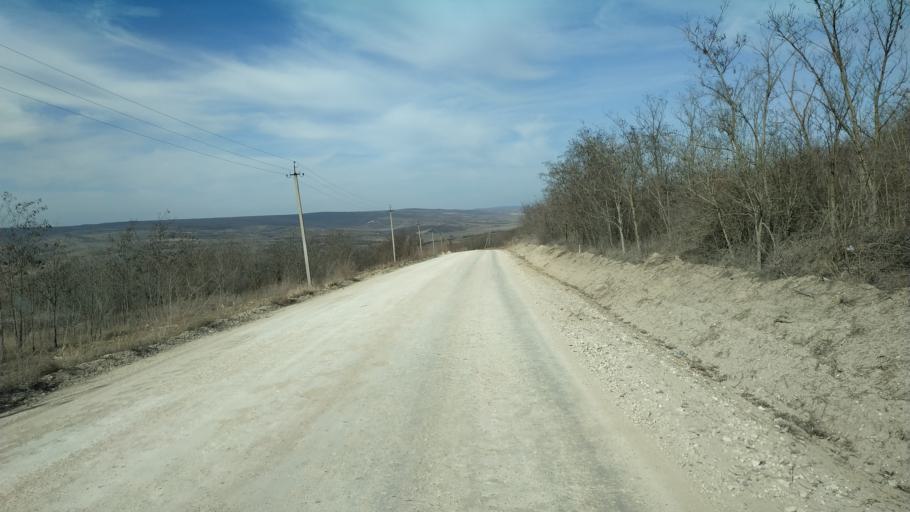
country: MD
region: Nisporeni
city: Nisporeni
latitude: 46.9696
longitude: 28.1990
